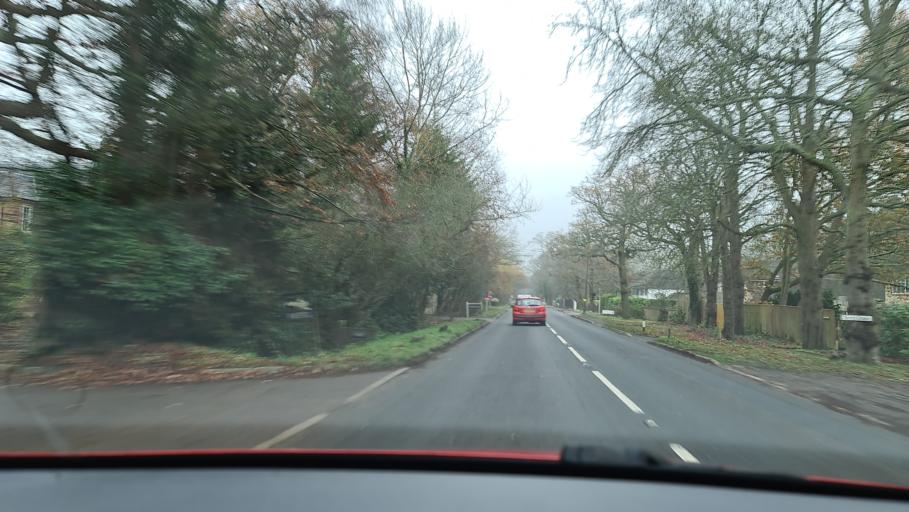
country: GB
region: England
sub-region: Surrey
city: Leatherhead
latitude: 51.3248
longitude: -0.3508
